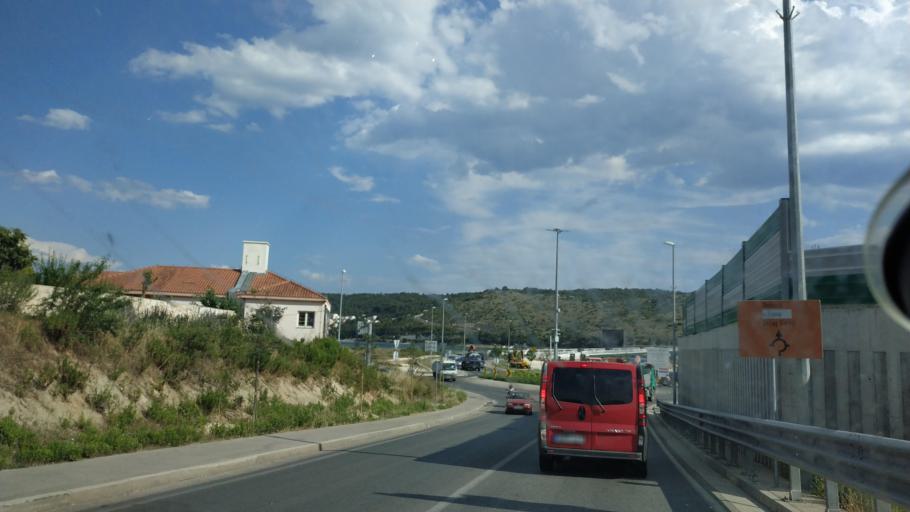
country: HR
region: Splitsko-Dalmatinska
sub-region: Grad Trogir
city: Trogir
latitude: 43.5234
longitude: 16.2639
